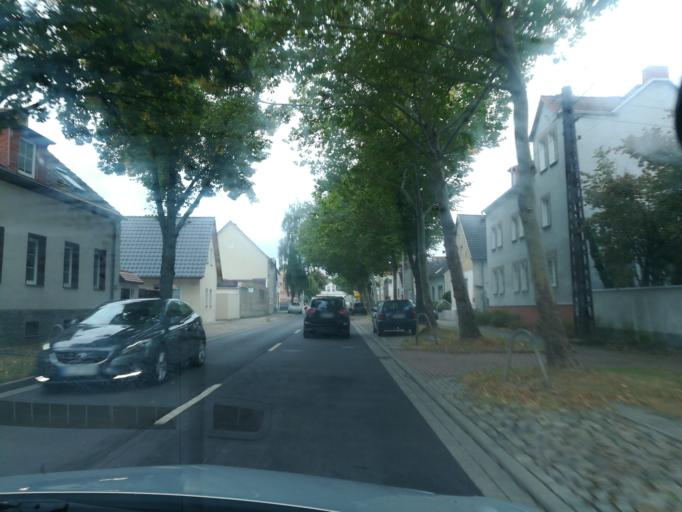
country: DE
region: Saxony-Anhalt
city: Diesdorf
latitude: 52.1575
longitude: 11.5729
